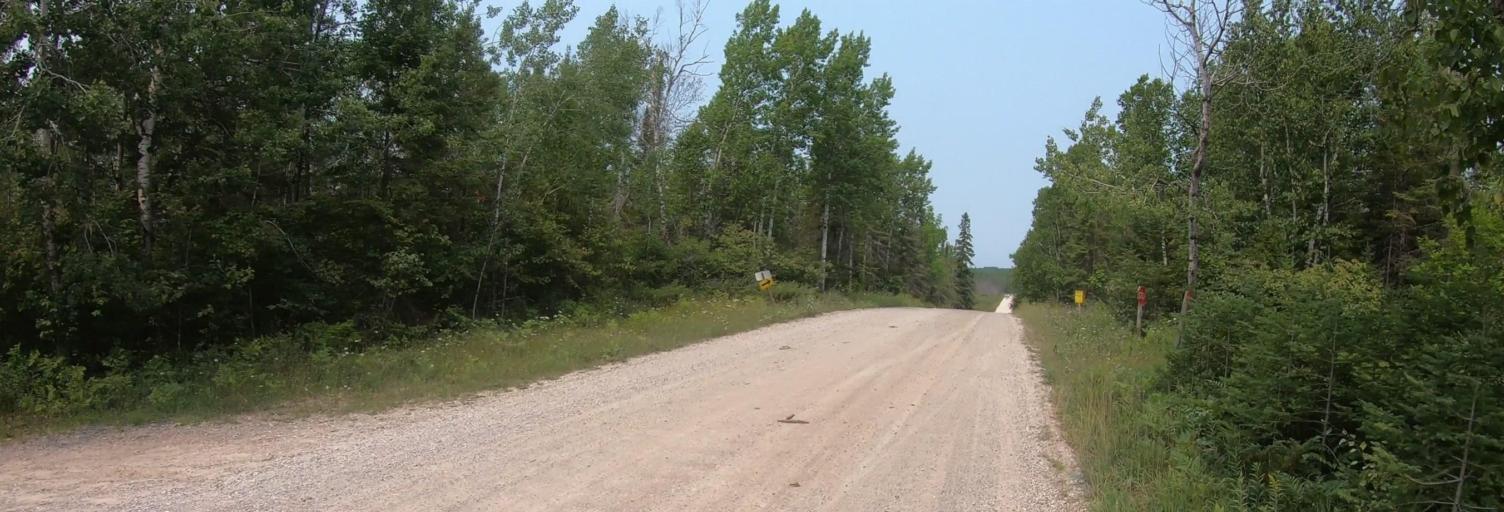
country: CA
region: Ontario
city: Thessalon
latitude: 46.0674
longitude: -83.6646
